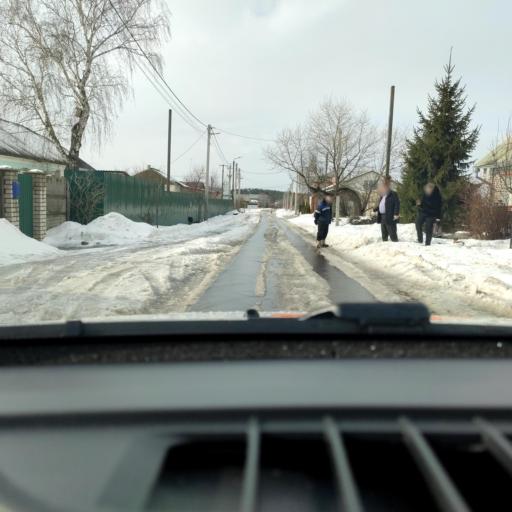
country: RU
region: Voronezj
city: Podgornoye
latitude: 51.7684
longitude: 39.1058
